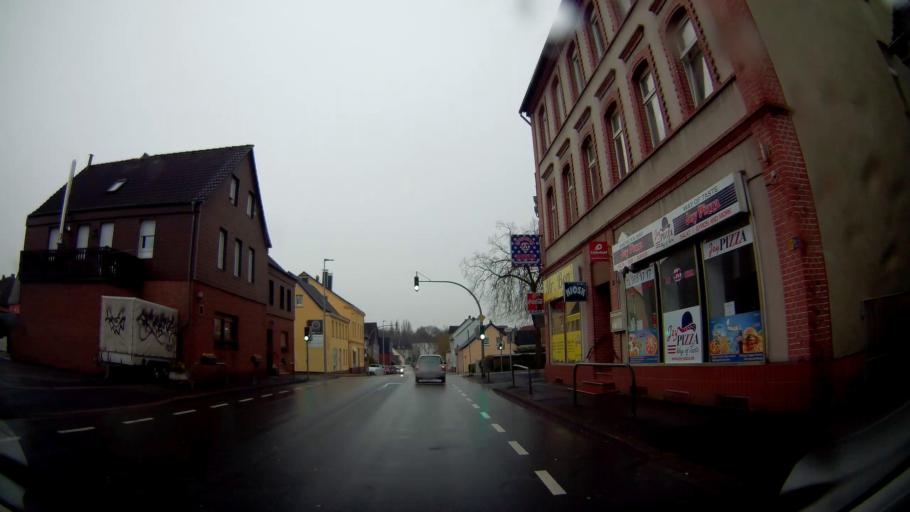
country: DE
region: North Rhine-Westphalia
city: Castrop-Rauxel
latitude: 51.5257
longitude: 7.3651
